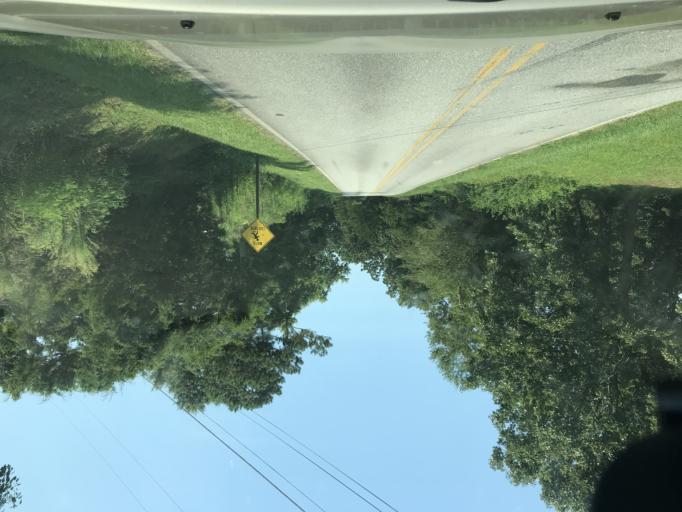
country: US
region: Georgia
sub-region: Dawson County
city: Dawsonville
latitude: 34.3328
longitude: -84.0794
